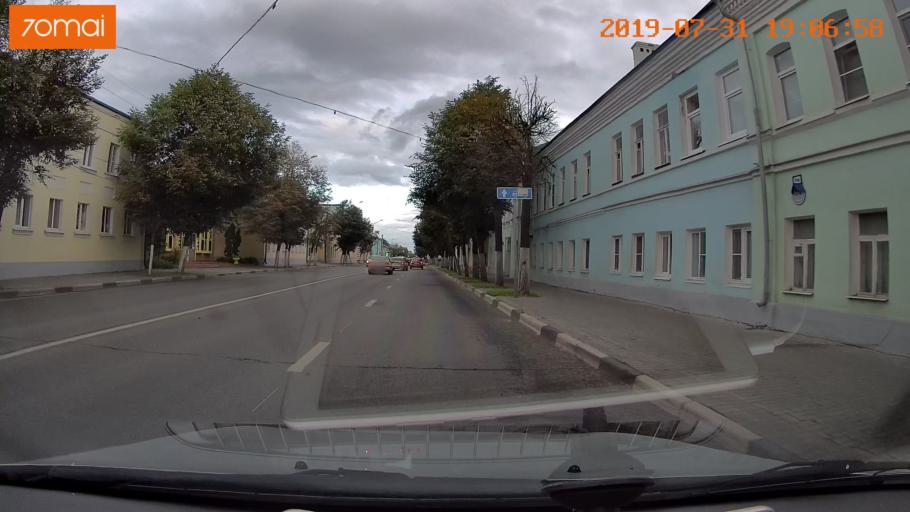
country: RU
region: Moskovskaya
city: Kolomna
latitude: 55.0997
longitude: 38.7580
